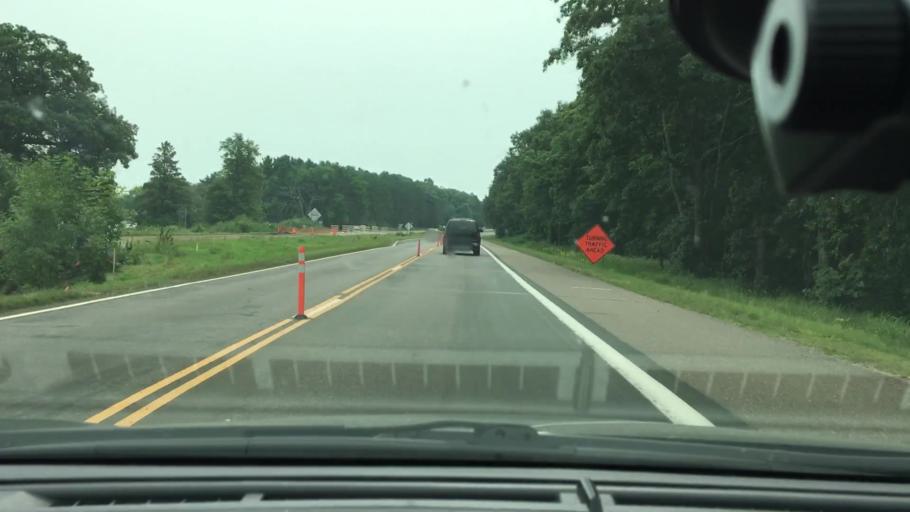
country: US
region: Minnesota
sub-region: Mille Lacs County
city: Vineland
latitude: 46.2874
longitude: -93.8240
